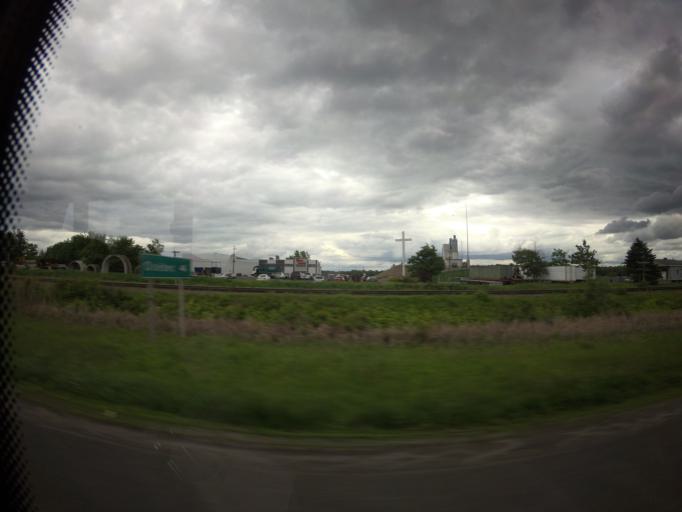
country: CA
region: Quebec
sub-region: Chaudiere-Appalaches
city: Saint-Antoine-de-Tilly
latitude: 46.5488
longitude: -71.6082
